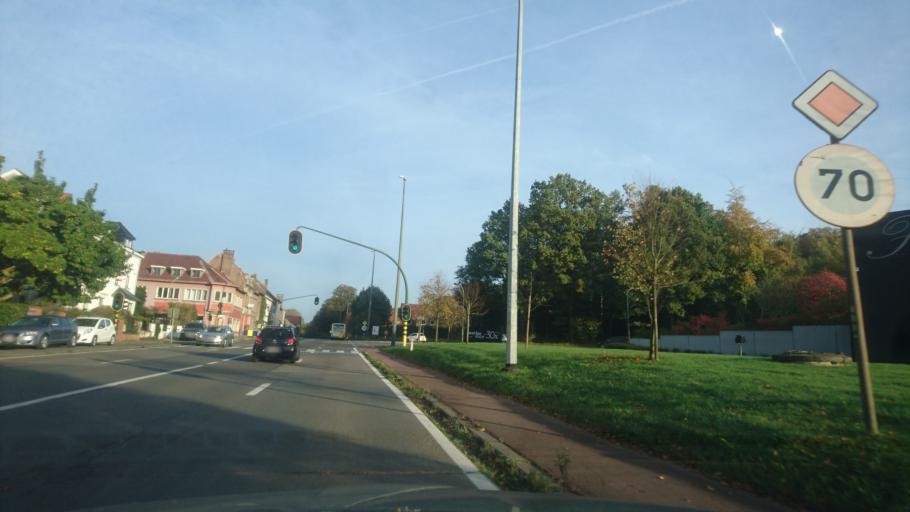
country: BE
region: Wallonia
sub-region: Province du Brabant Wallon
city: Waterloo
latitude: 50.7482
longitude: 4.3944
